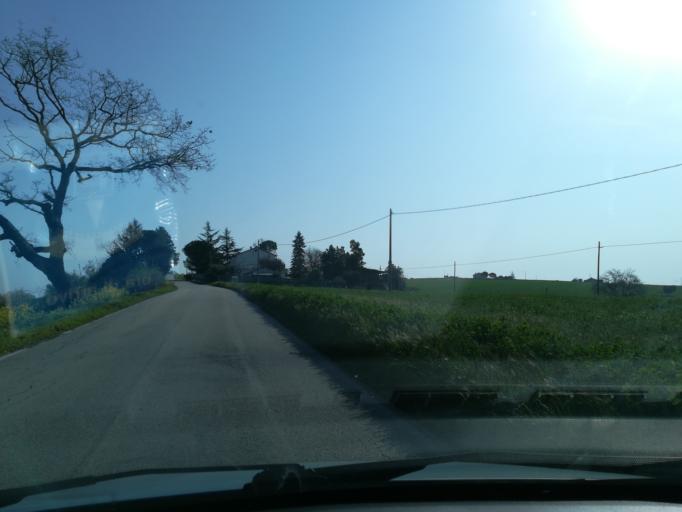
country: IT
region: The Marches
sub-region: Provincia di Macerata
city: Villa Potenza
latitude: 43.3314
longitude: 13.4574
